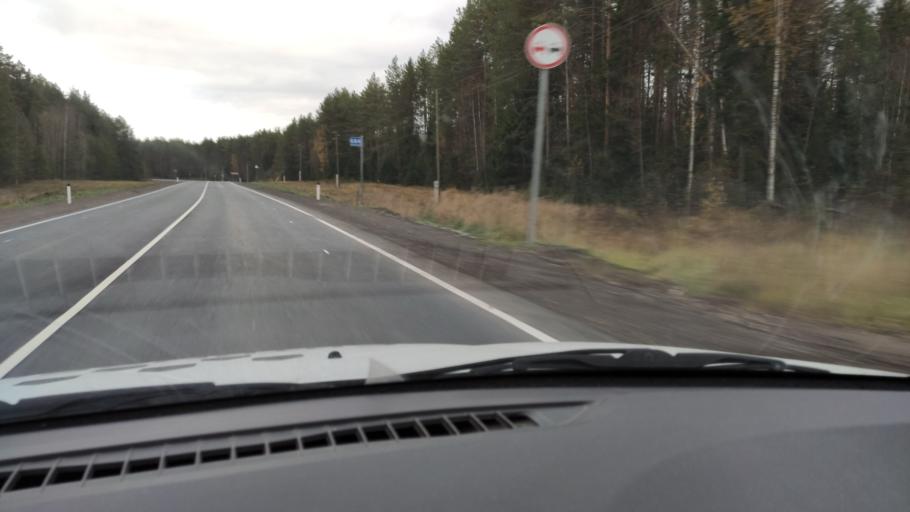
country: RU
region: Kirov
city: Belaya Kholunitsa
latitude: 58.8418
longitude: 50.7746
